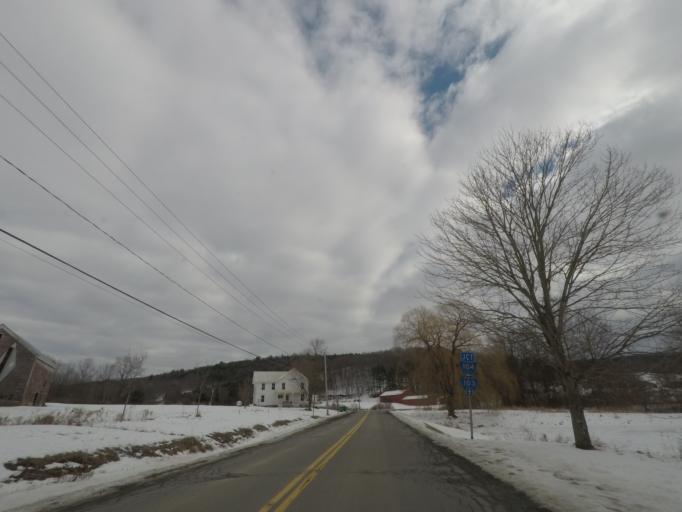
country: US
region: New York
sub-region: Rensselaer County
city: Hoosick Falls
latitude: 42.8993
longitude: -73.4237
